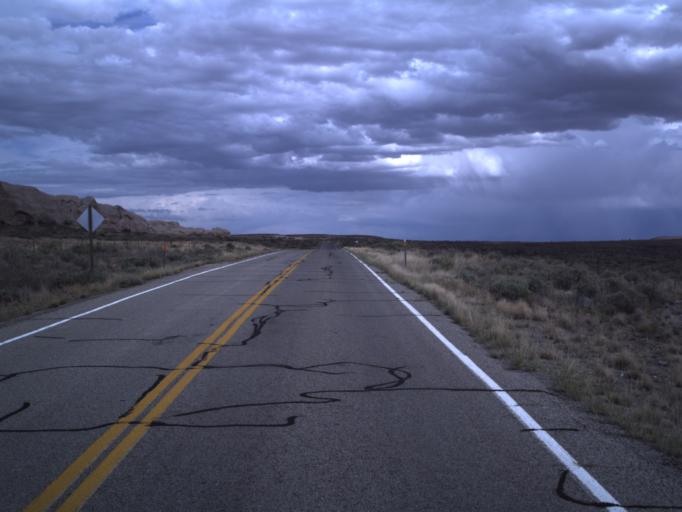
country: US
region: Utah
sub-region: San Juan County
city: Blanding
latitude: 37.2823
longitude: -109.5065
